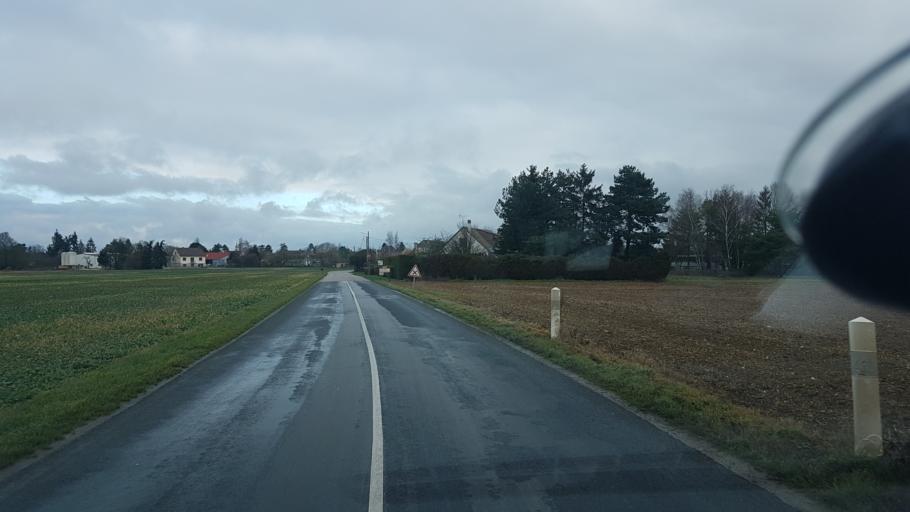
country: FR
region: Ile-de-France
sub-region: Departement de Seine-et-Marne
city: Souppes-sur-Loing
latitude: 48.2024
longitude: 2.7791
